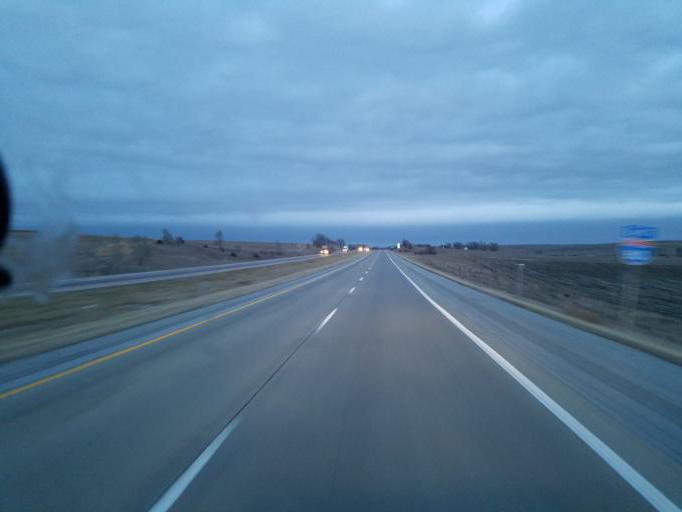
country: US
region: Iowa
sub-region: Cass County
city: Atlantic
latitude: 41.4972
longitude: -95.1092
